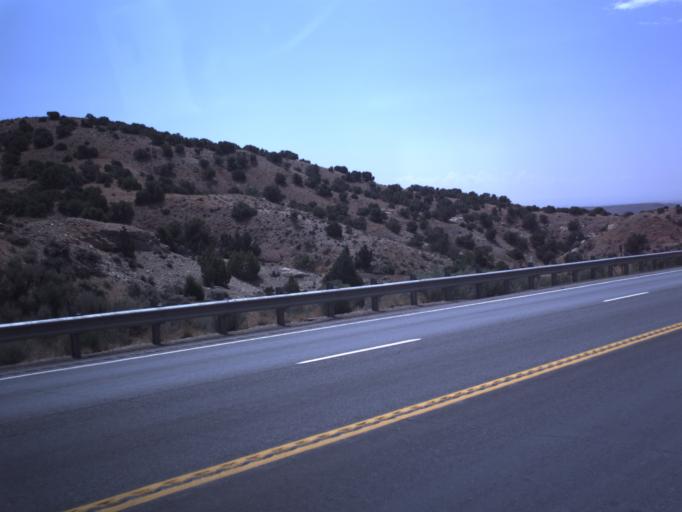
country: US
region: Utah
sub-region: Uintah County
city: Maeser
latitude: 40.4077
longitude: -109.5888
